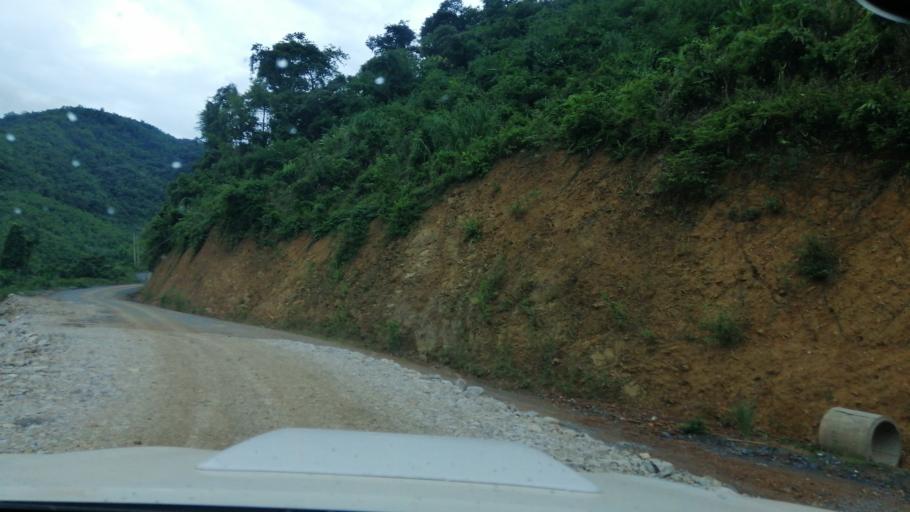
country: LA
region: Xiagnabouli
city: Sainyabuli
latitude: 19.1816
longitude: 101.7972
